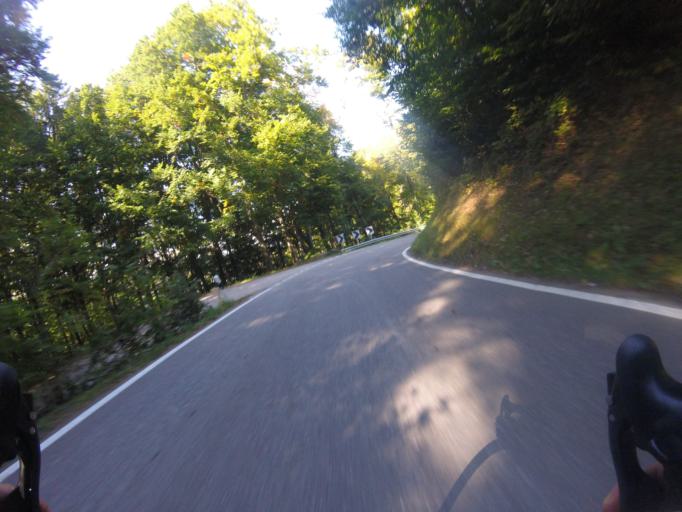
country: CH
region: Bern
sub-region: Bern-Mittelland District
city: Toffen
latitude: 46.8714
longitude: 7.5084
